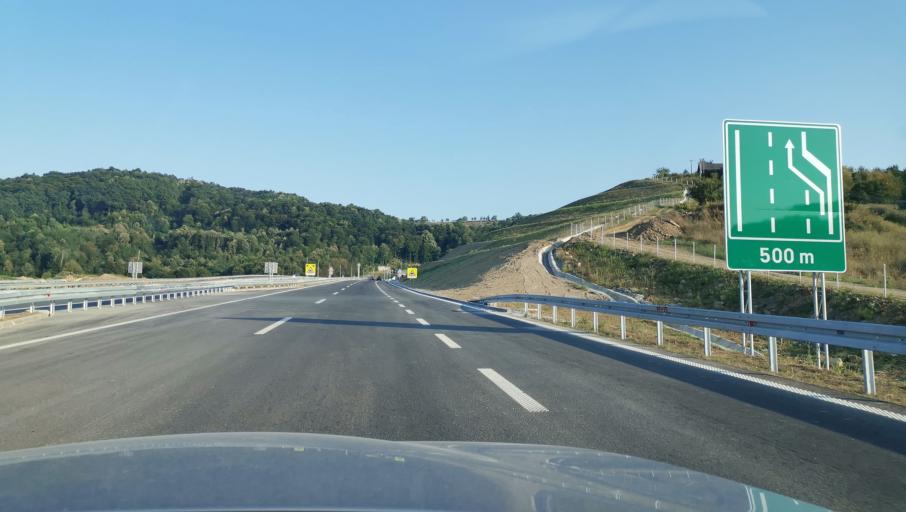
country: RS
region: Central Serbia
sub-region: Kolubarski Okrug
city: Ljig
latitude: 44.2160
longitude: 20.2590
